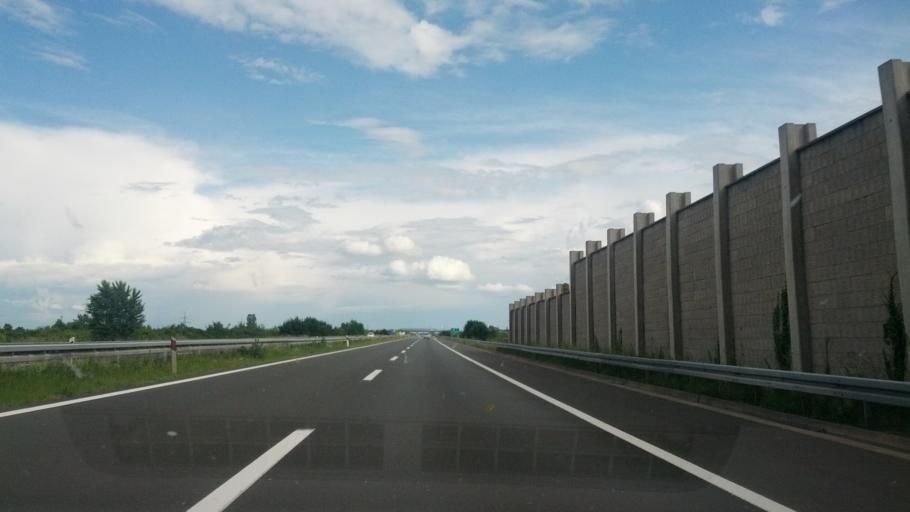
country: HR
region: Zagrebacka
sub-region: Grad Samobor
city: Samobor
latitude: 45.8125
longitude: 15.7640
